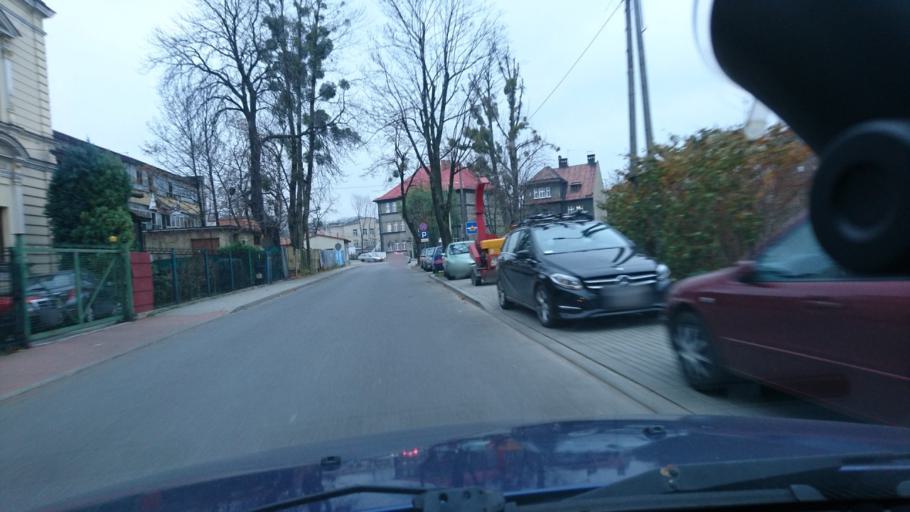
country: PL
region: Silesian Voivodeship
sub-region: Bielsko-Biala
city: Bielsko-Biala
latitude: 49.8179
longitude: 19.0503
